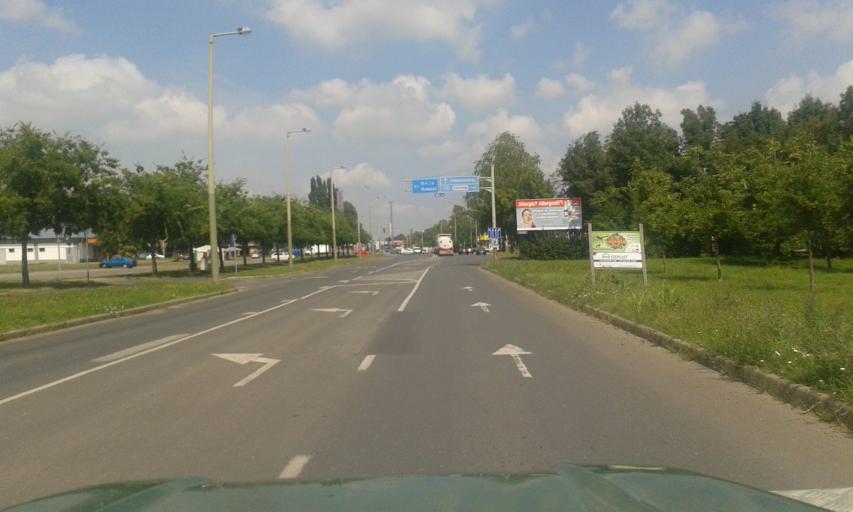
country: HU
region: Csongrad
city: Szeged
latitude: 46.2516
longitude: 20.1230
